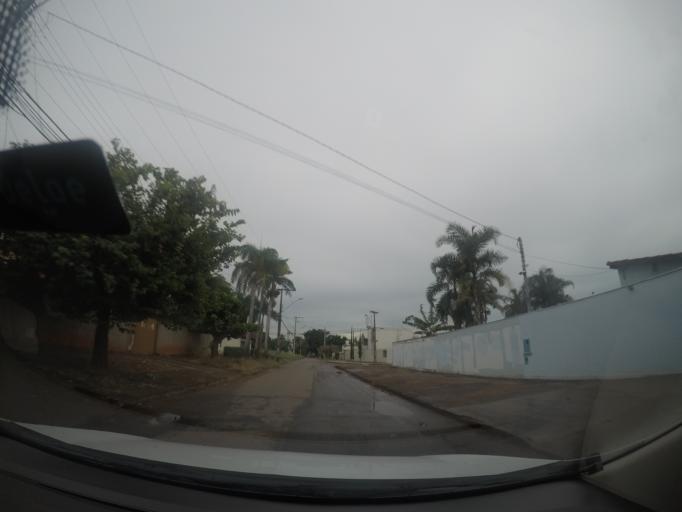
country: BR
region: Goias
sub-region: Goiania
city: Goiania
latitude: -16.6374
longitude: -49.2420
